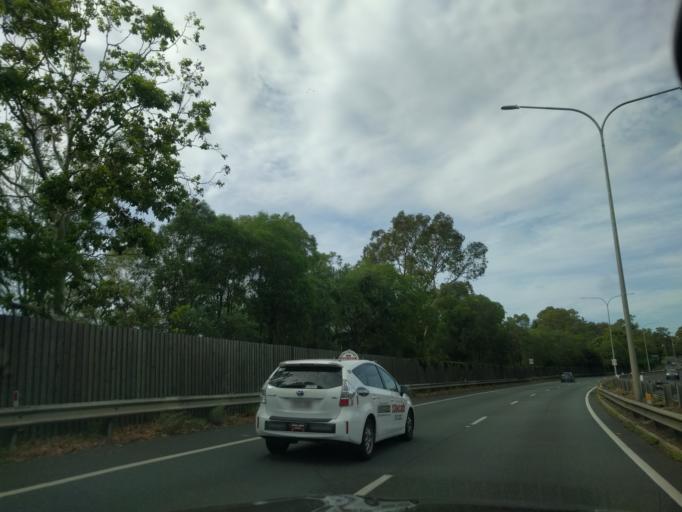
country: AU
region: Queensland
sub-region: Brisbane
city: Taringa
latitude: -27.5072
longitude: 152.9624
